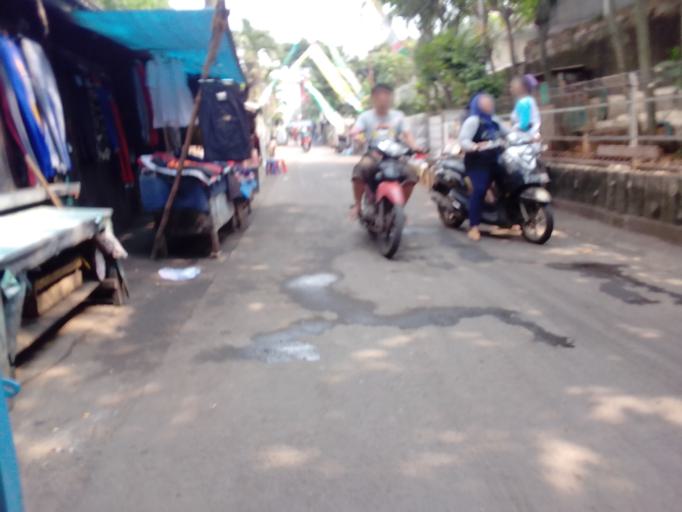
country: ID
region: Jakarta Raya
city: Jakarta
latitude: -6.2097
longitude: 106.7952
